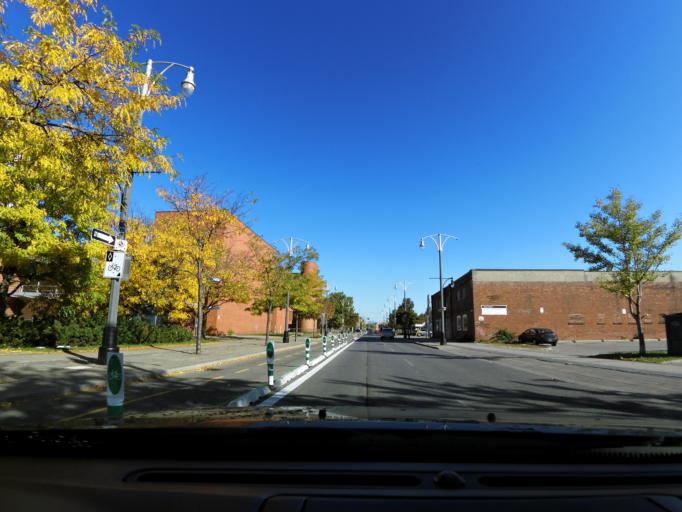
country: CA
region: Ontario
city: Hamilton
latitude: 43.2602
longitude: -79.8730
